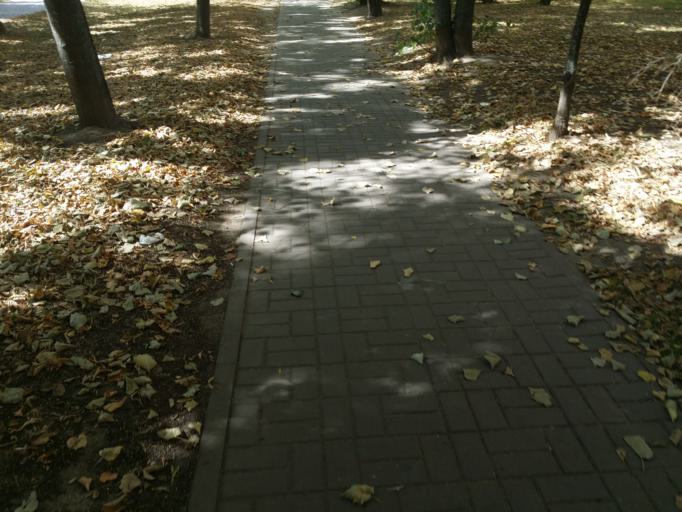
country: BY
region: Minsk
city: Minsk
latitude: 53.9406
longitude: 27.6009
